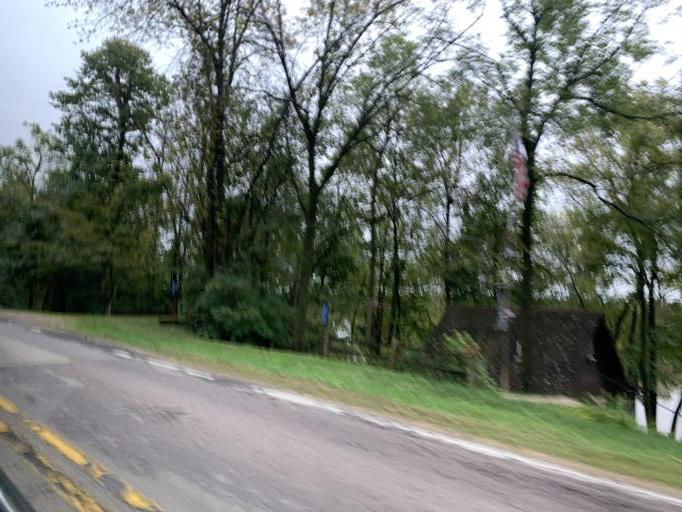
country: US
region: Wisconsin
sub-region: Grant County
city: Muscoda
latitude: 43.2026
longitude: -90.4238
